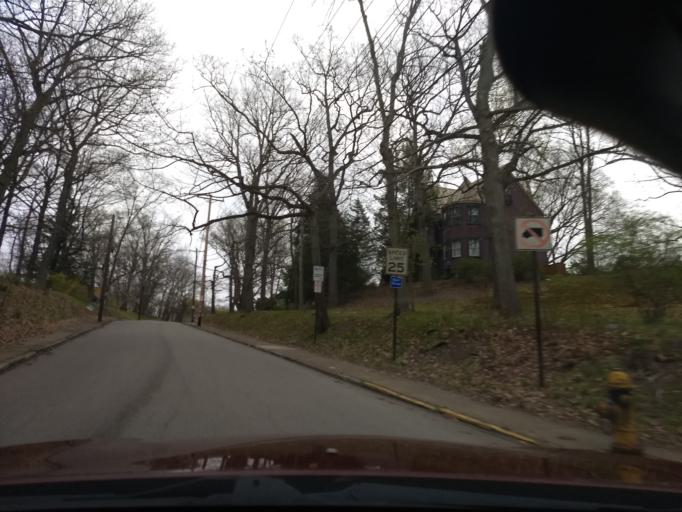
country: US
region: Pennsylvania
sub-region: Allegheny County
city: Ingram
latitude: 40.4465
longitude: -80.0786
